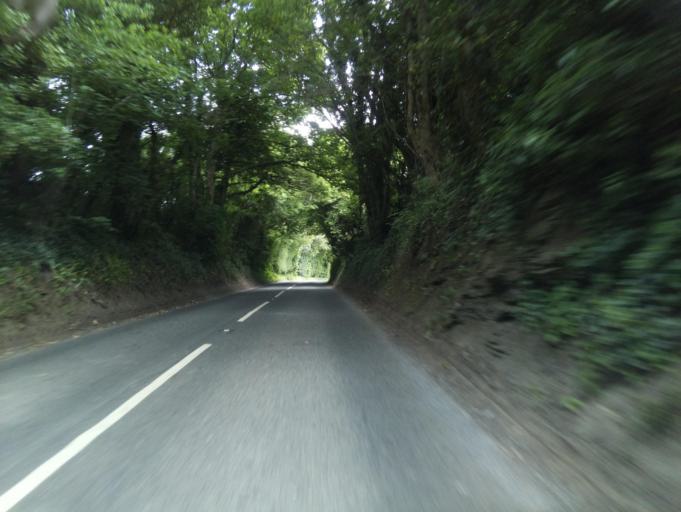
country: GB
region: England
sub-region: Somerset
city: Milborne Port
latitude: 51.0163
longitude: -2.4709
